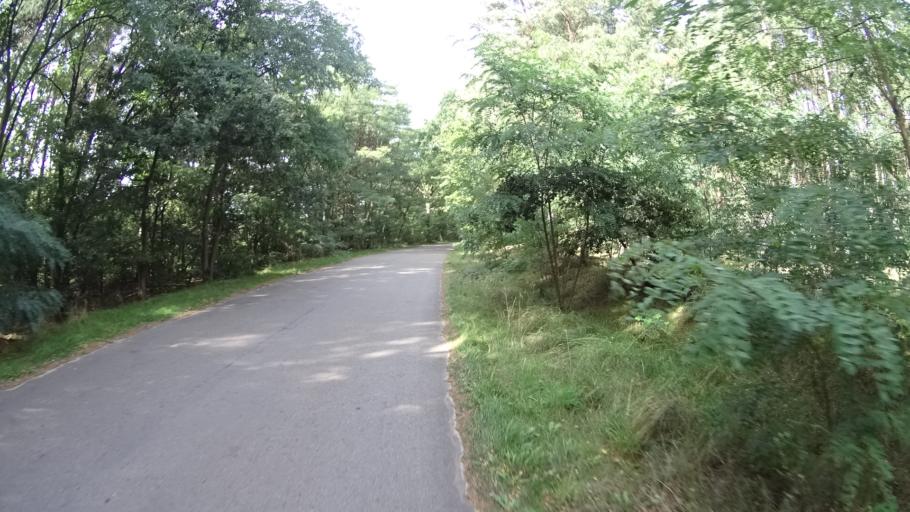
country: PL
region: Masovian Voivodeship
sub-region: Powiat legionowski
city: Serock
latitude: 52.4908
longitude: 21.0872
